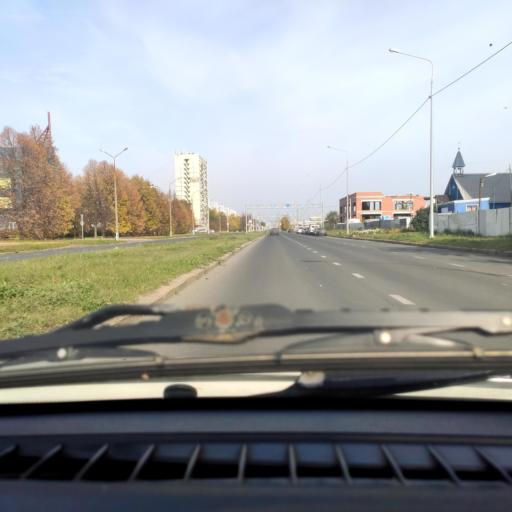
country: RU
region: Samara
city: Tol'yatti
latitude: 53.5050
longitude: 49.2703
